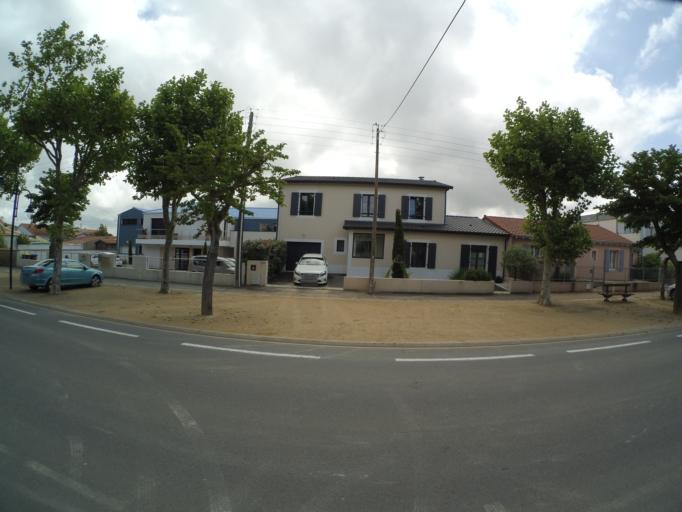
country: FR
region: Poitou-Charentes
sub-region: Departement de la Charente-Maritime
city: Chatelaillon-Plage
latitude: 46.0652
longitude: -1.0917
